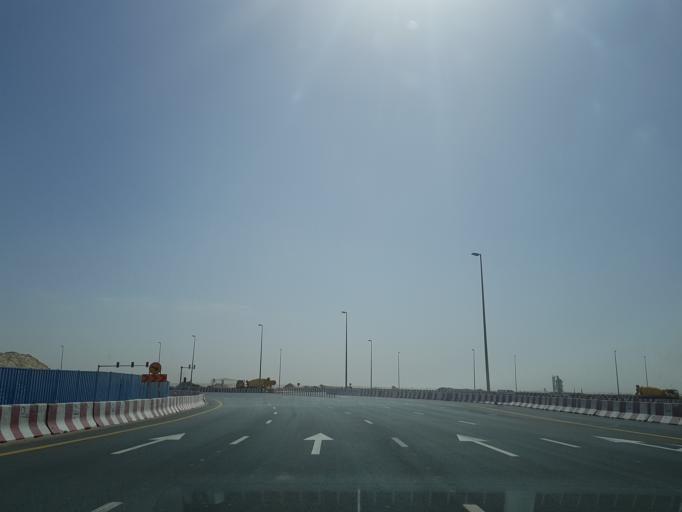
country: AE
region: Dubai
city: Dubai
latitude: 24.9615
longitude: 55.1789
